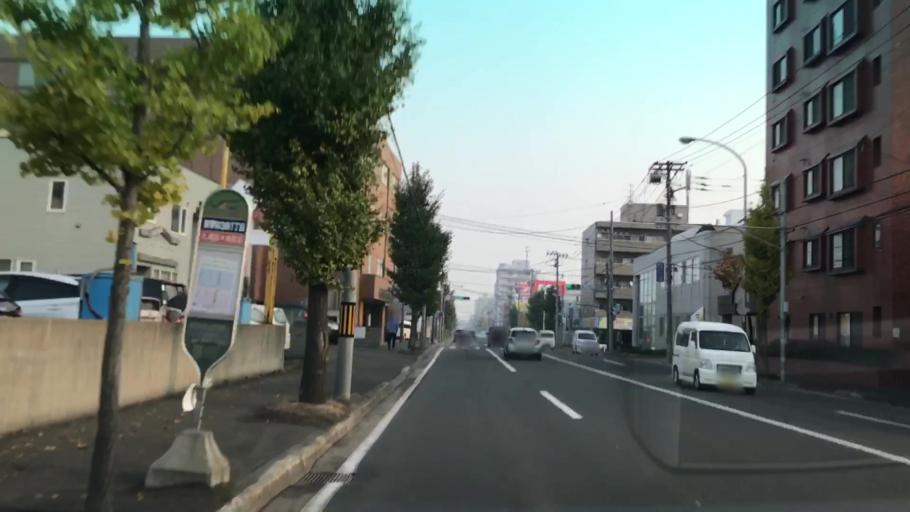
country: JP
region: Hokkaido
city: Sapporo
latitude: 43.1043
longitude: 141.3303
